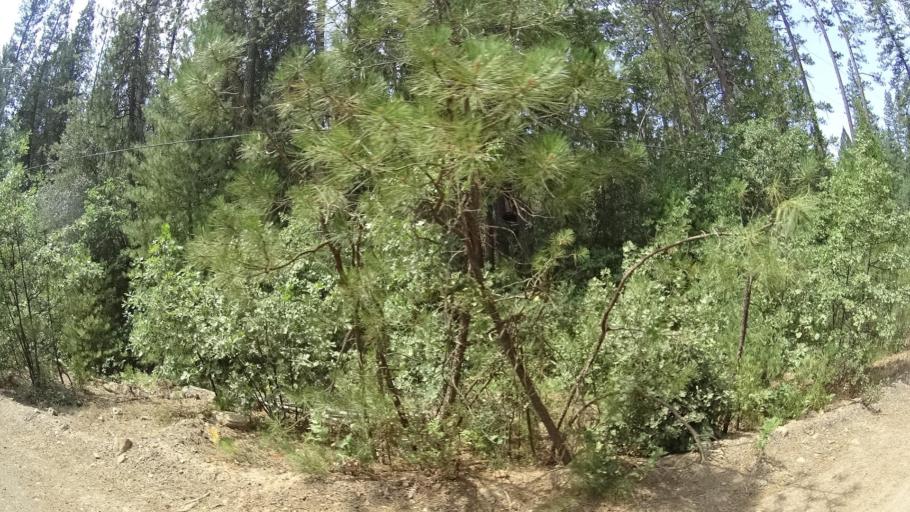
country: US
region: California
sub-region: Mariposa County
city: Midpines
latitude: 37.7373
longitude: -120.0827
